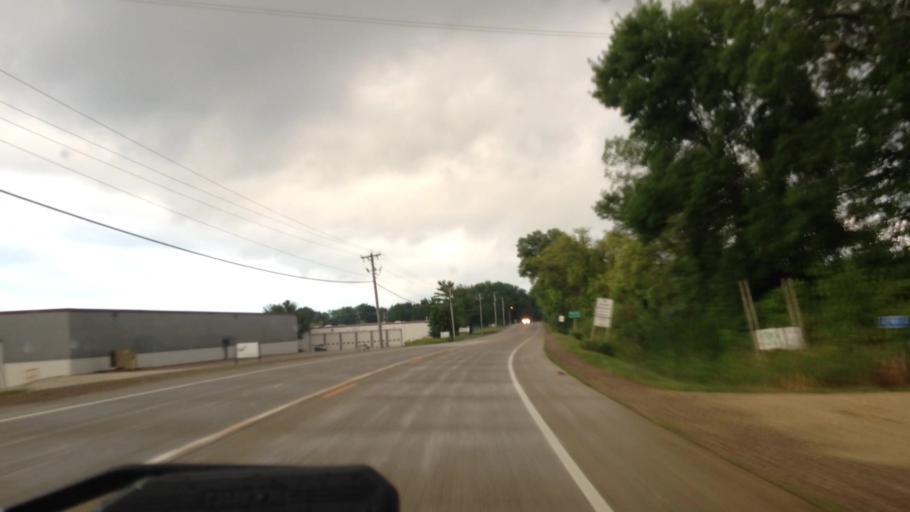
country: US
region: Wisconsin
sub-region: Dodge County
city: Mayville
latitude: 43.4830
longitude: -88.5529
